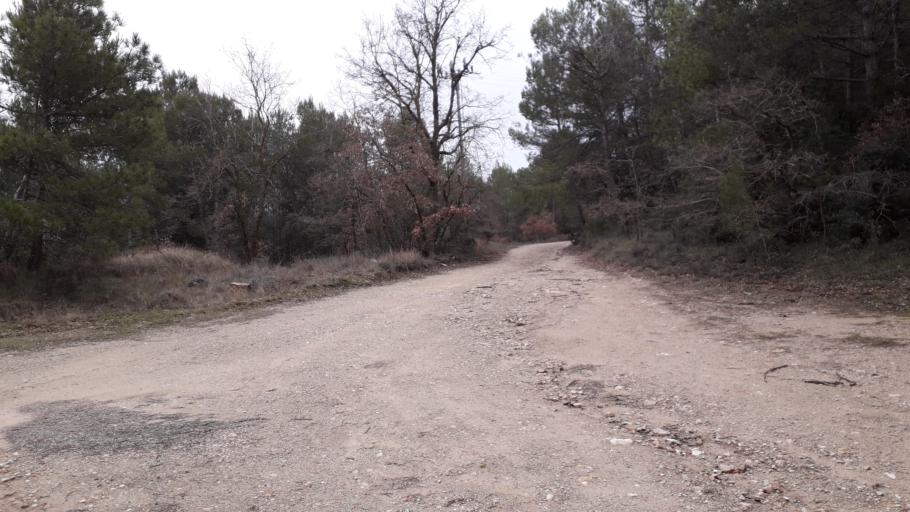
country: ES
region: Catalonia
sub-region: Provincia de Barcelona
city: Bellprat
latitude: 41.4869
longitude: 1.4526
